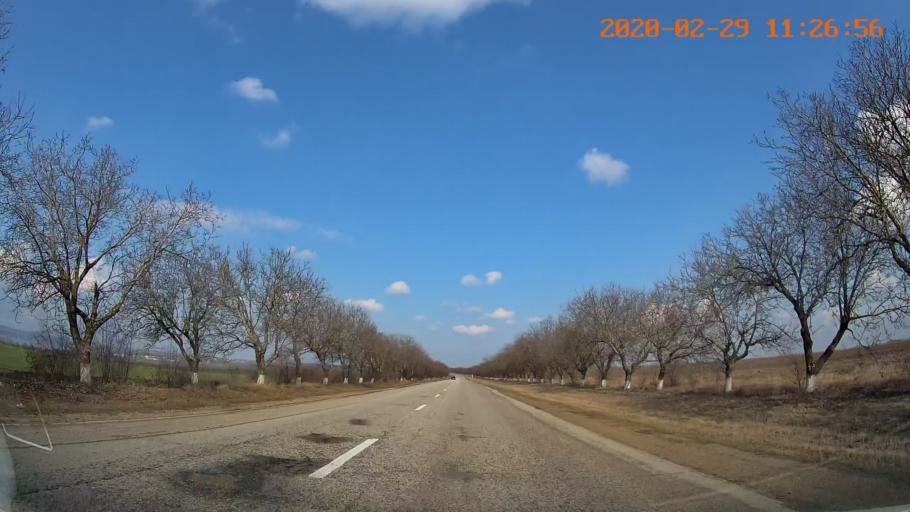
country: MD
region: Telenesti
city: Cocieri
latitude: 47.4603
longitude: 29.1441
